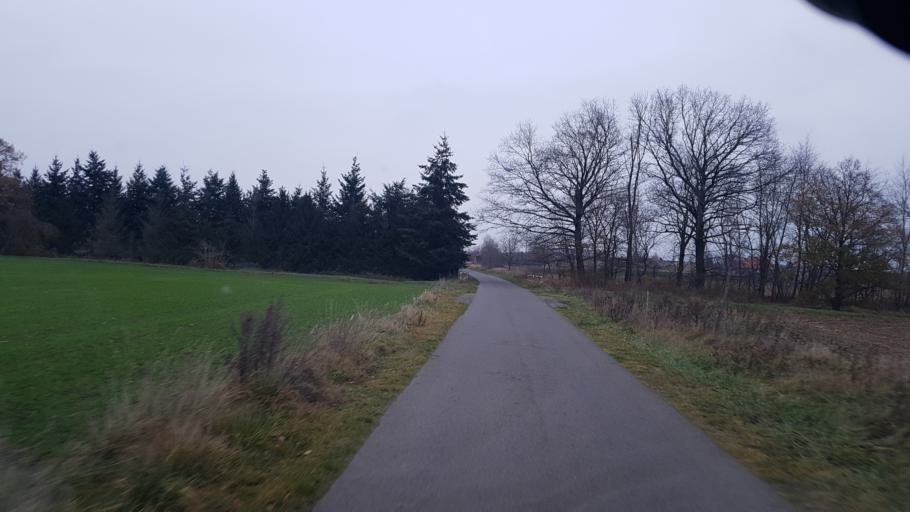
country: DE
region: Brandenburg
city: Schenkendobern
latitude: 51.9321
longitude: 14.5606
